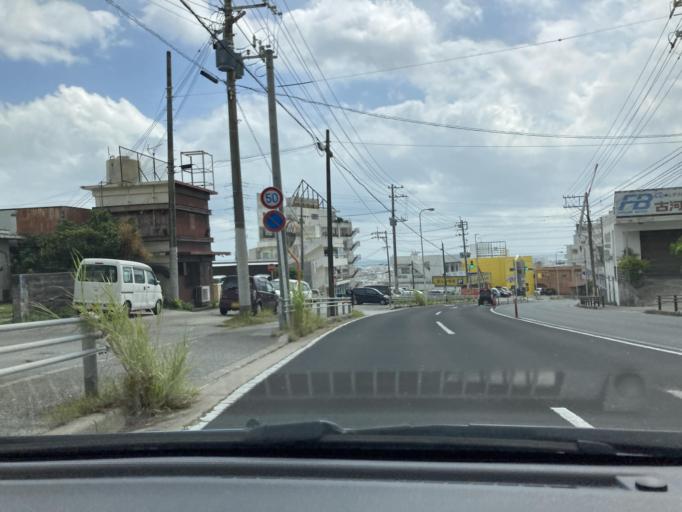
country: JP
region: Okinawa
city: Okinawa
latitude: 26.3317
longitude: 127.8221
